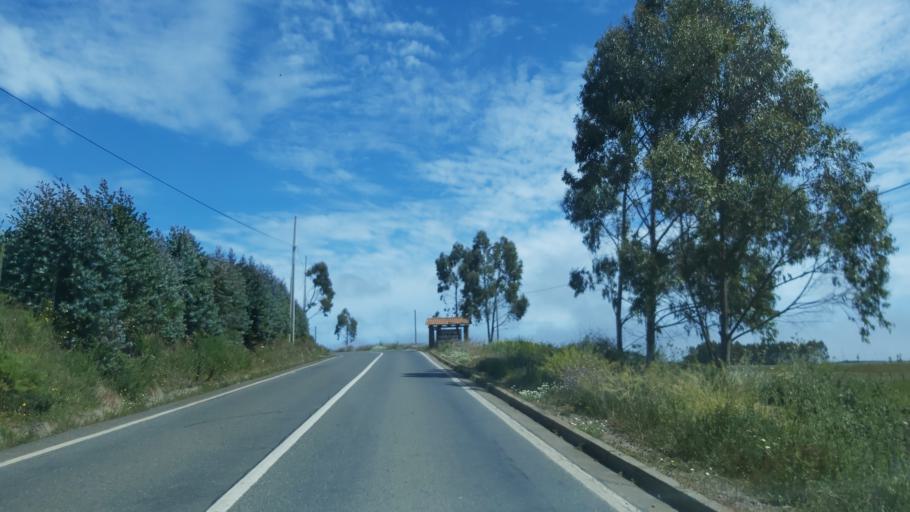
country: CL
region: Maule
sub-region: Provincia de Talca
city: Constitucion
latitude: -35.5748
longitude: -72.6028
